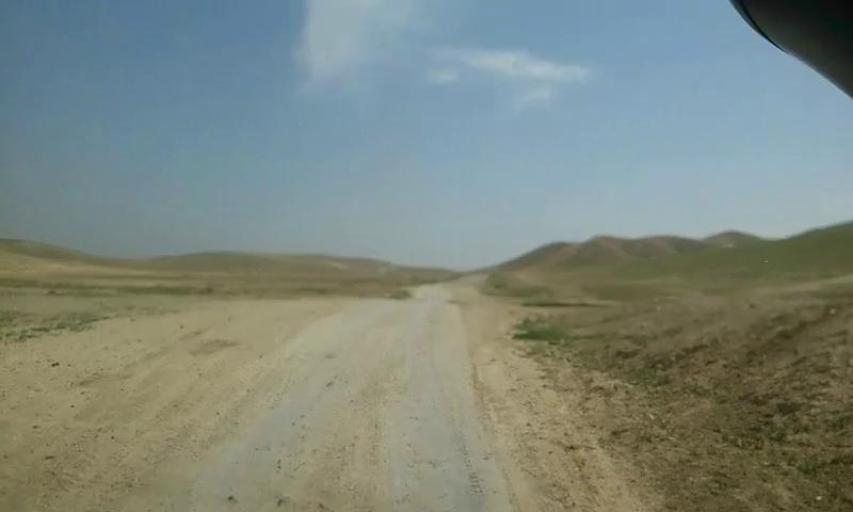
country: PS
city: `Arab ar Rashaydah
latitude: 31.5319
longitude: 35.2852
